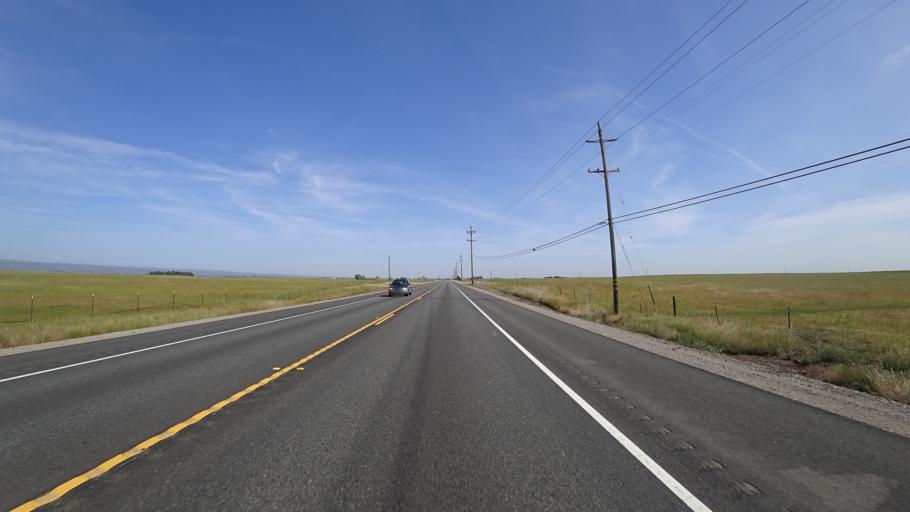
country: US
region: California
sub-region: Glenn County
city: Hamilton City
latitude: 39.8679
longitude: -121.9647
